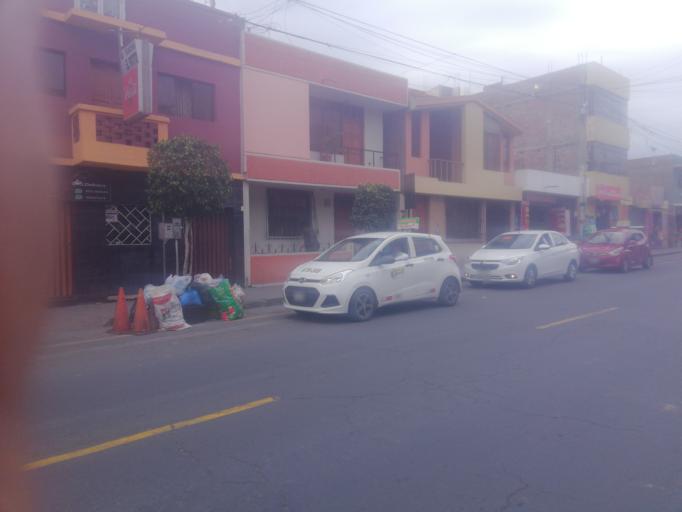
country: PE
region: Arequipa
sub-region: Provincia de Arequipa
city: Tiabaya
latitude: -16.4489
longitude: -71.5905
